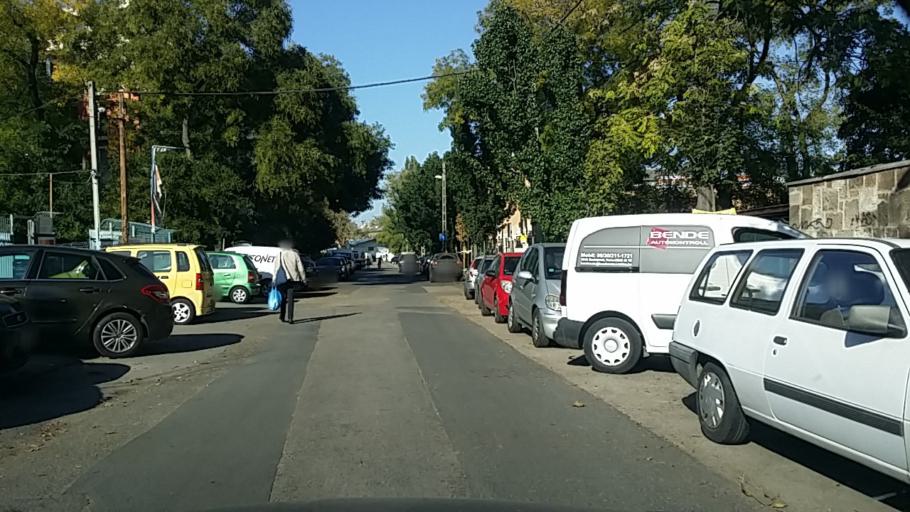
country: HU
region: Budapest
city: Budapest XI. keruelet
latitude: 47.4698
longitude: 19.0238
